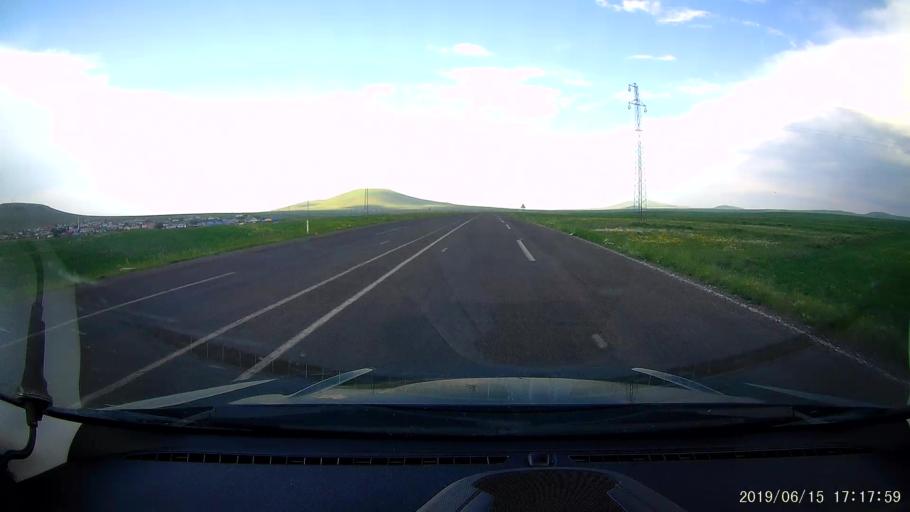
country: TR
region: Kars
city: Kars
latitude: 40.6141
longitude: 43.2489
